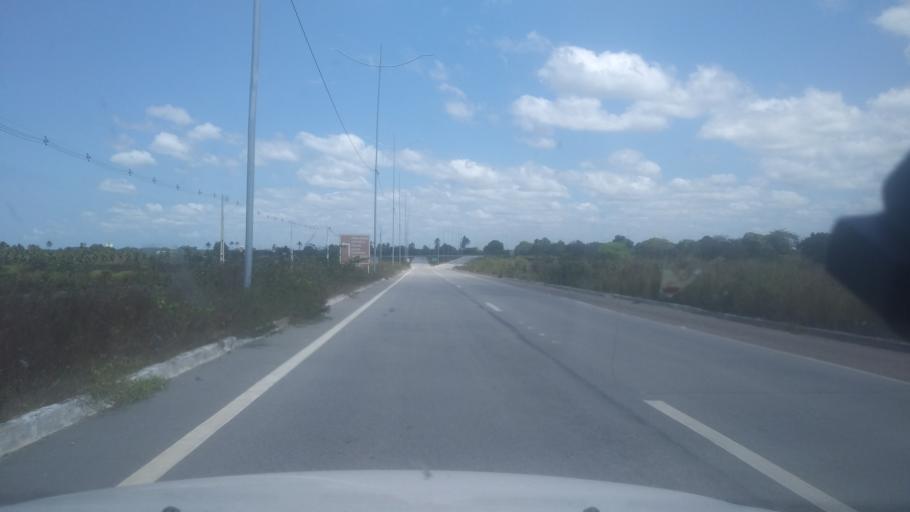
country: BR
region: Rio Grande do Norte
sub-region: Macaiba
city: Macaiba
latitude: -5.8636
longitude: -35.3783
